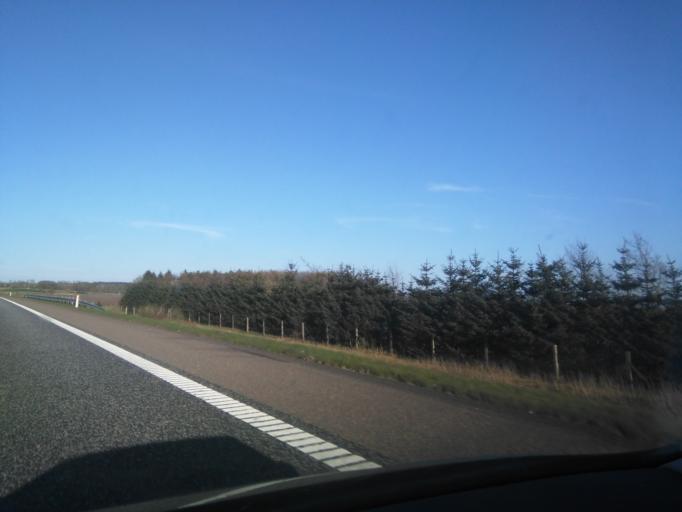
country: DK
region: Central Jutland
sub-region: Ikast-Brande Kommune
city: Ikast
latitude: 56.1173
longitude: 9.1606
